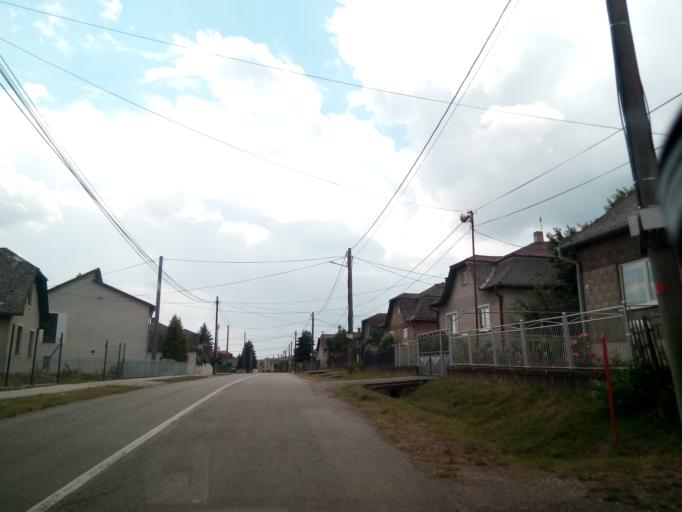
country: SK
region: Kosicky
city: Secovce
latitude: 48.5874
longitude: 21.5666
